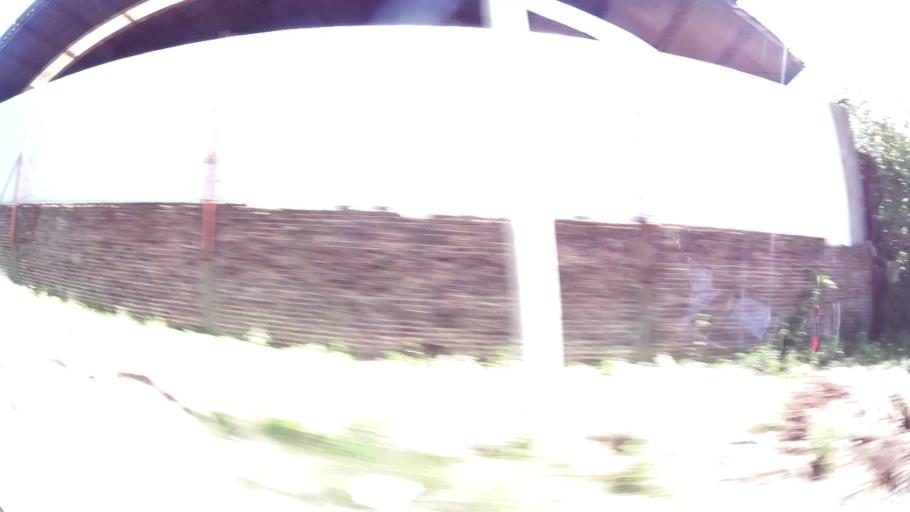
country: AR
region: Buenos Aires
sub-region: Partido de Tigre
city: Tigre
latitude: -34.4986
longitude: -58.6075
